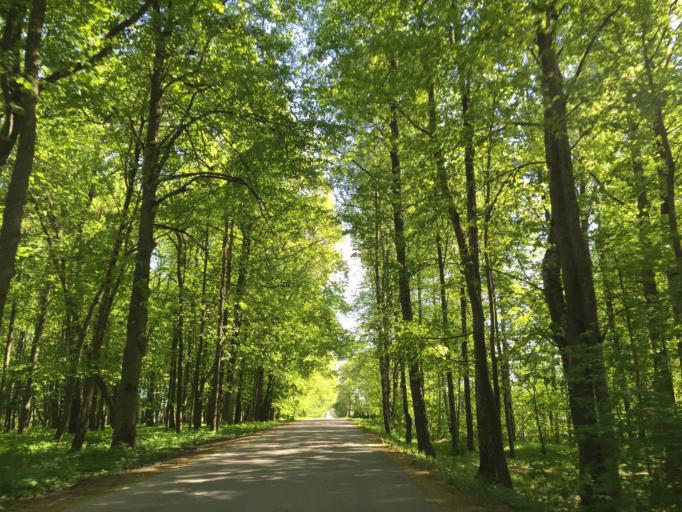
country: LV
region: Rundales
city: Pilsrundale
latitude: 56.3770
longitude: 23.9276
